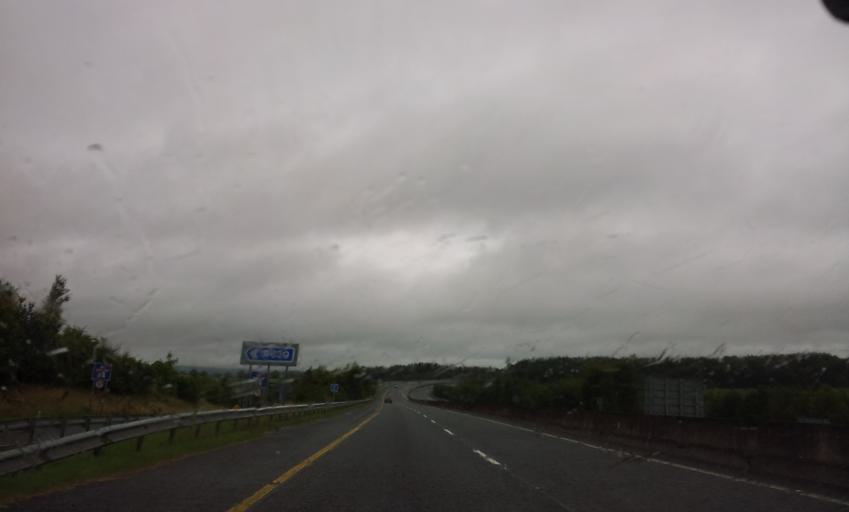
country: IE
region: Munster
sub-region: County Cork
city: Fermoy
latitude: 52.1119
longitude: -8.2735
